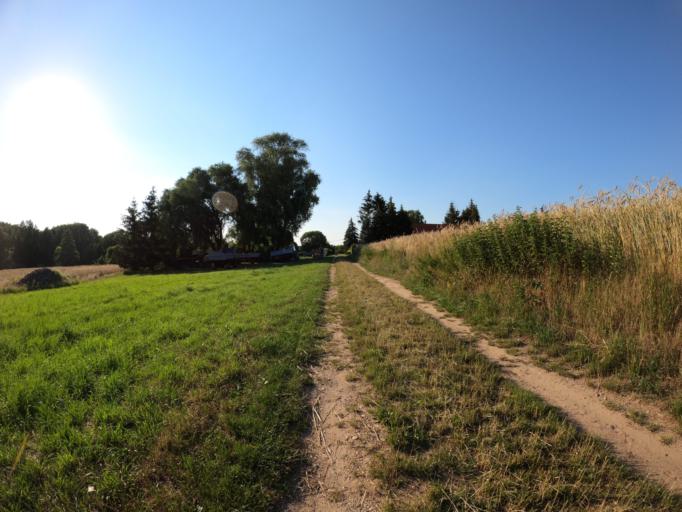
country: DE
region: Brandenburg
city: Tantow
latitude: 53.2507
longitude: 14.3640
